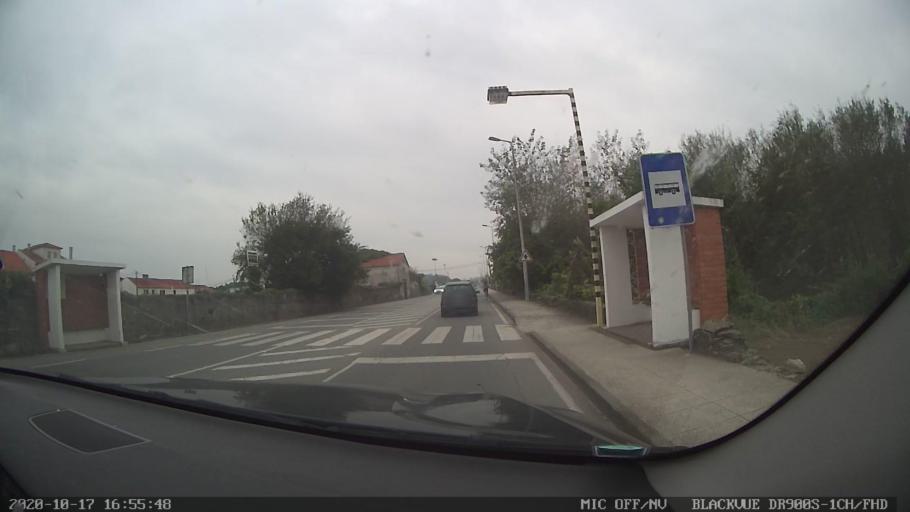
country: PT
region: Braga
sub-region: Esposende
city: Apulia
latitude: 41.5098
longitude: -8.7677
